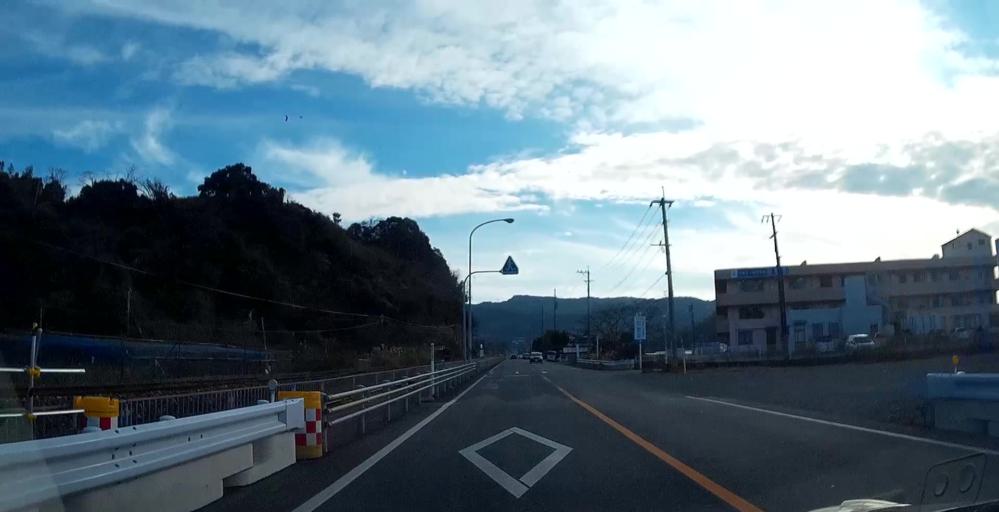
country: JP
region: Kumamoto
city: Uto
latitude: 32.6804
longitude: 130.5536
